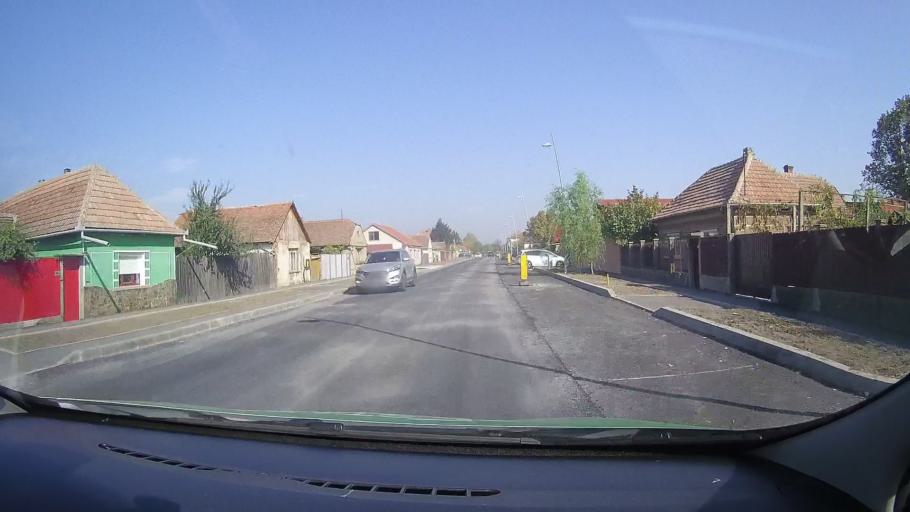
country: RO
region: Bihor
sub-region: Municipiul Salonta
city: Salonta
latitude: 46.7939
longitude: 21.6648
